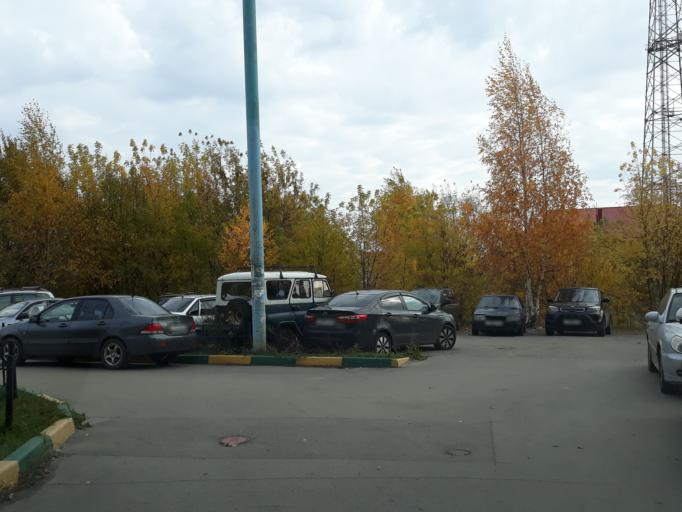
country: RU
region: Nizjnij Novgorod
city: Nizhniy Novgorod
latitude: 56.2405
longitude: 43.9804
